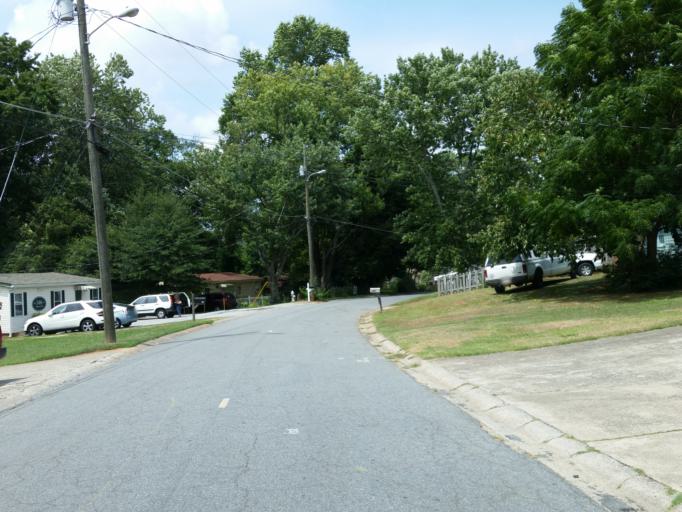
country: US
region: Georgia
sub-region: Cobb County
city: Marietta
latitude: 33.9435
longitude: -84.5190
